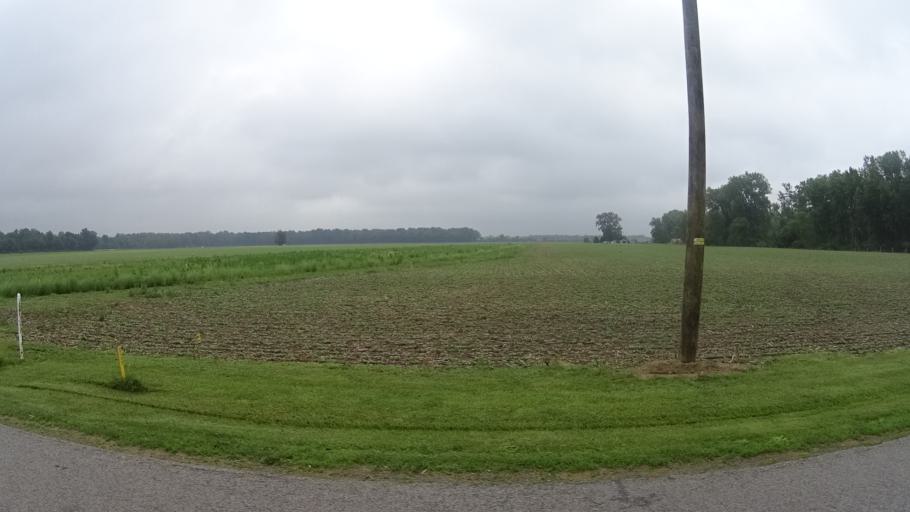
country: US
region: Ohio
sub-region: Huron County
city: Bellevue
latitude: 41.3511
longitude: -82.8169
